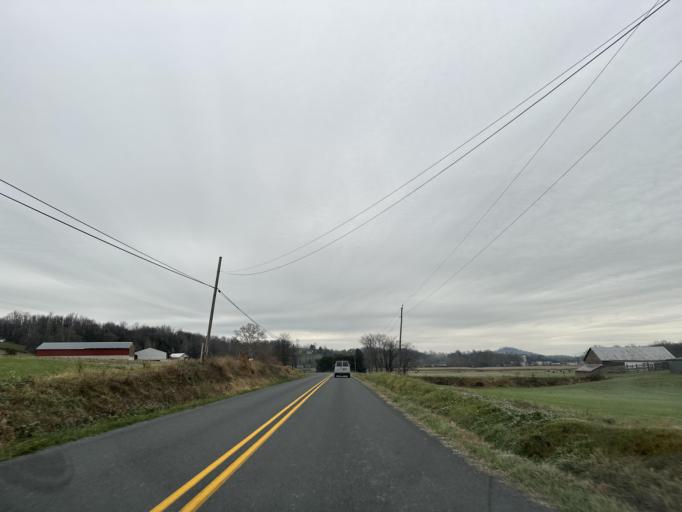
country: US
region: Virginia
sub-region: Rockingham County
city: Bridgewater
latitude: 38.3925
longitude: -79.0620
